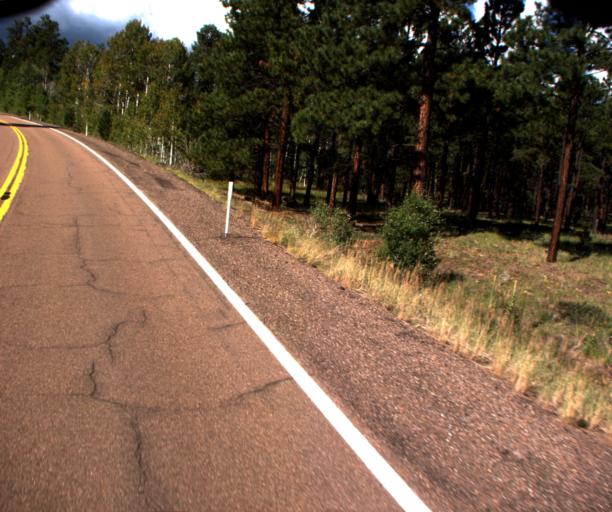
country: US
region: Arizona
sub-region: Apache County
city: Eagar
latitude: 34.0694
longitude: -109.4854
